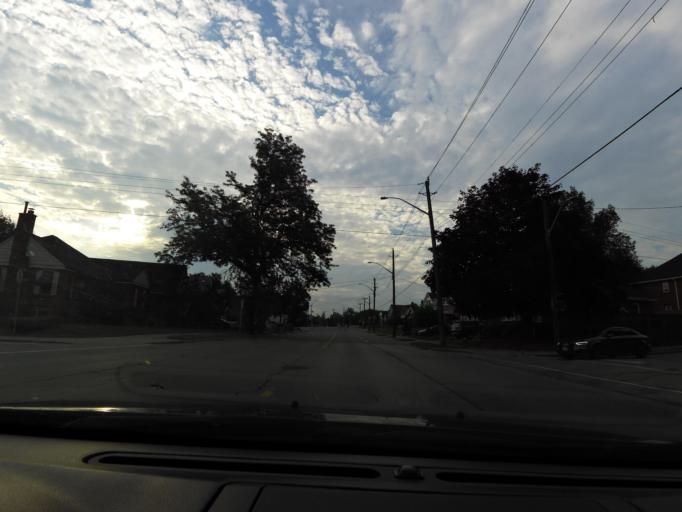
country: CA
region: Ontario
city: Hamilton
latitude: 43.2337
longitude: -79.8154
